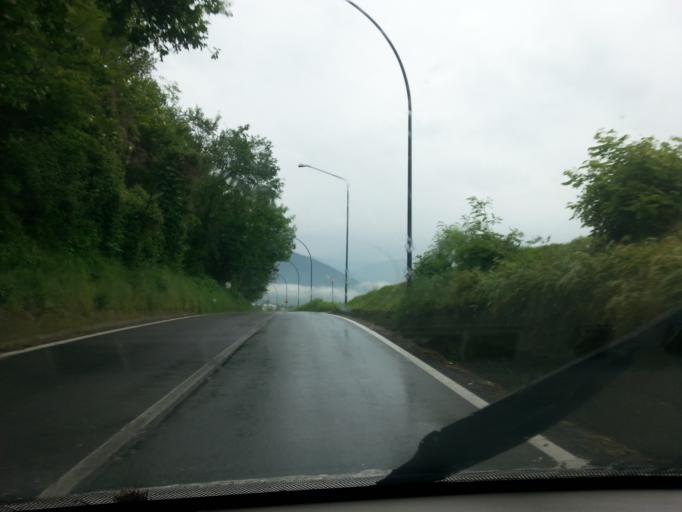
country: IT
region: Piedmont
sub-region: Provincia di Torino
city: Alpignano
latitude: 45.1003
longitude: 7.5157
